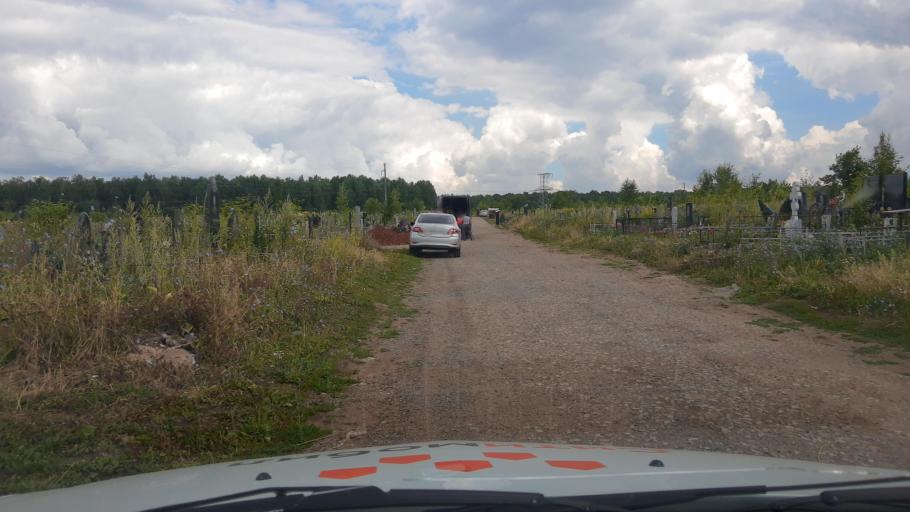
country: RU
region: Bashkortostan
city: Mikhaylovka
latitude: 54.8140
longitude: 55.8617
